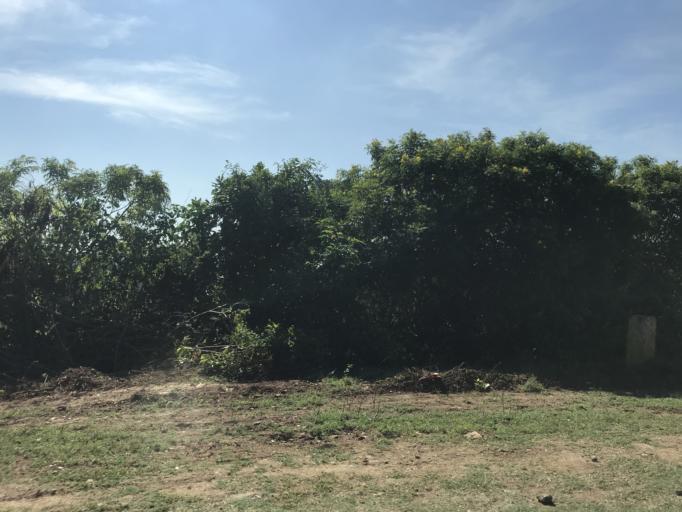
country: IN
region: Karnataka
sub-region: Mysore
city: Heggadadevankote
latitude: 12.0454
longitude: 76.3351
